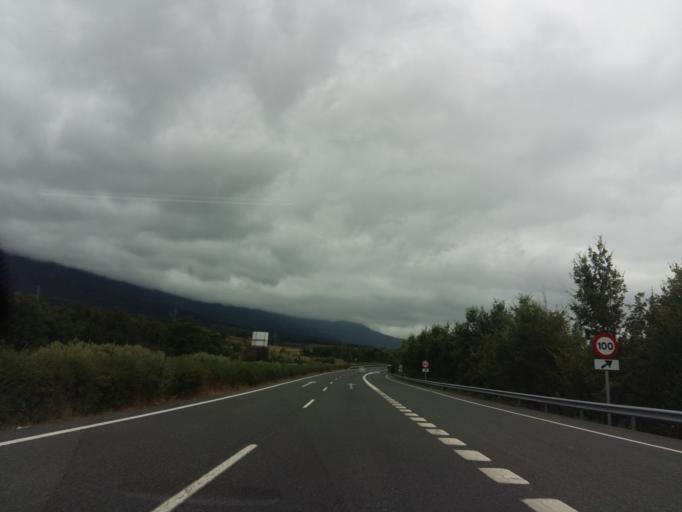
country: ES
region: Navarre
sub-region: Provincia de Navarra
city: Irurtzun
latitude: 42.9141
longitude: -1.8892
